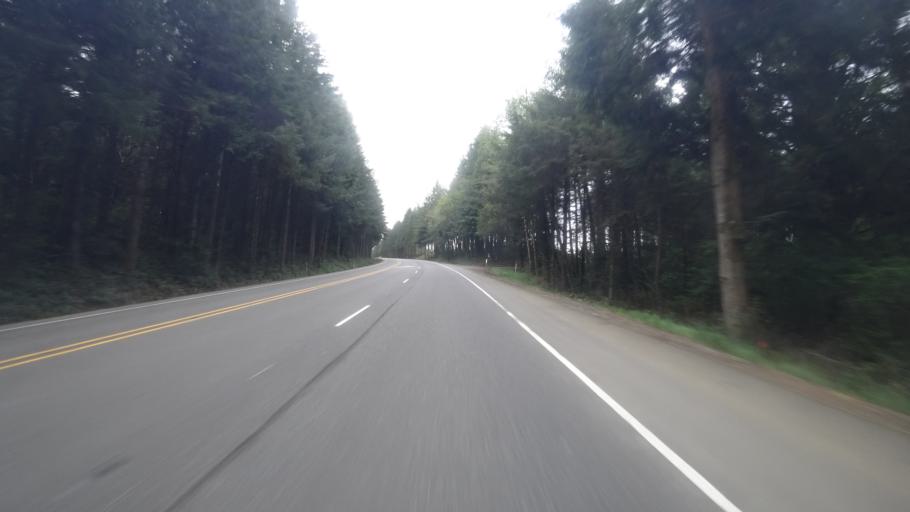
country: US
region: Oregon
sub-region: Coos County
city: Coquille
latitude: 43.2159
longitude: -124.3076
